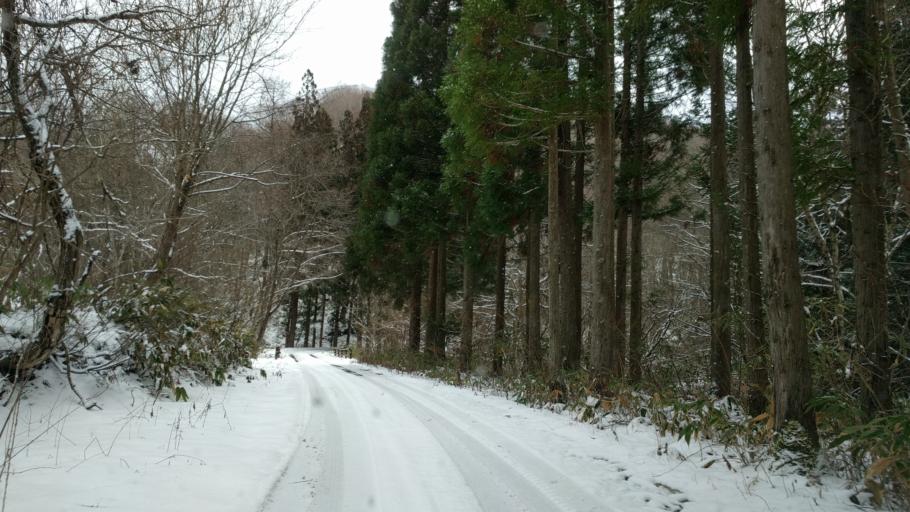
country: JP
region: Fukushima
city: Inawashiro
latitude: 37.3905
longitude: 140.0217
